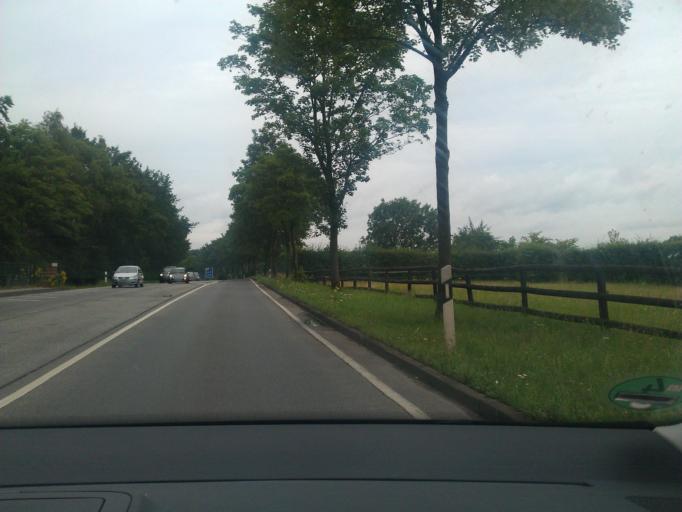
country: BE
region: Wallonia
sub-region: Province de Liege
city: Raeren
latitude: 50.7161
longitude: 6.1317
